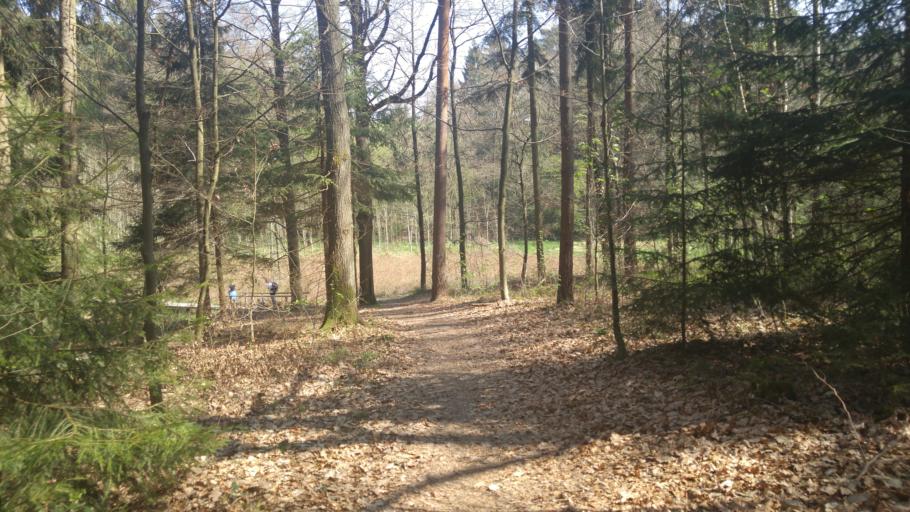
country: DE
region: Bavaria
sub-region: Regierungsbezirk Mittelfranken
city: Spardorf
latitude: 49.6157
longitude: 11.0457
